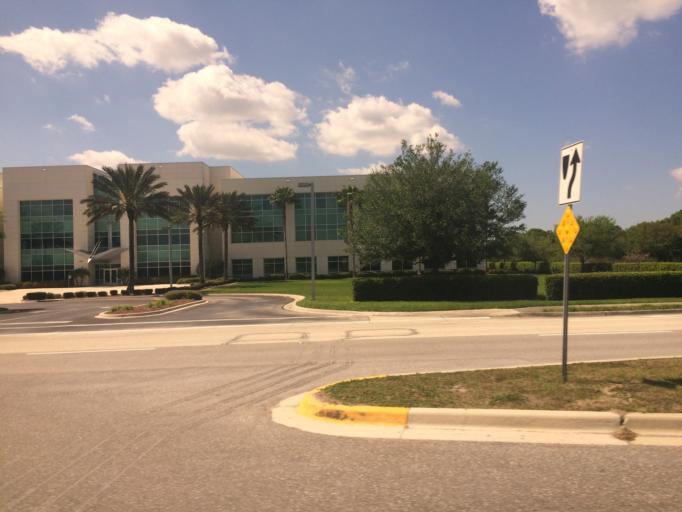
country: US
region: Florida
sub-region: Sarasota County
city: The Meadows
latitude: 27.4519
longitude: -82.4323
